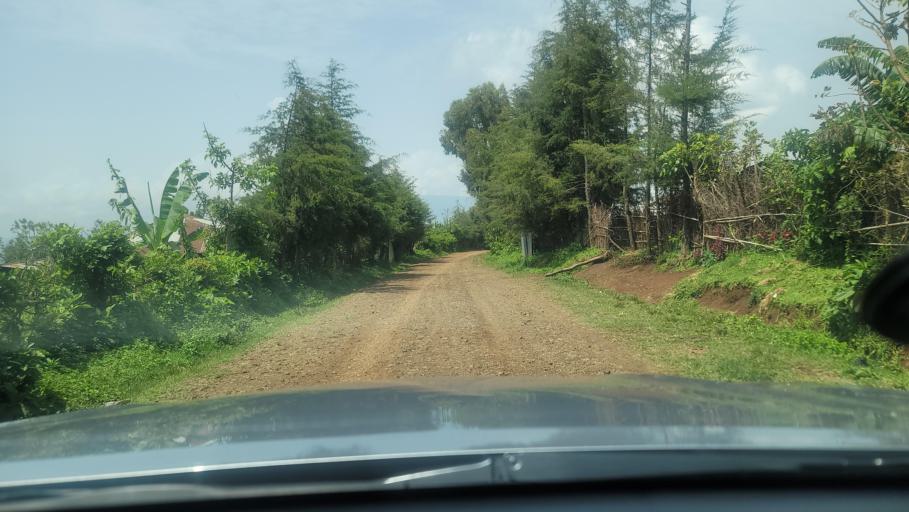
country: ET
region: Oromiya
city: Agaro
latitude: 7.8300
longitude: 36.4071
